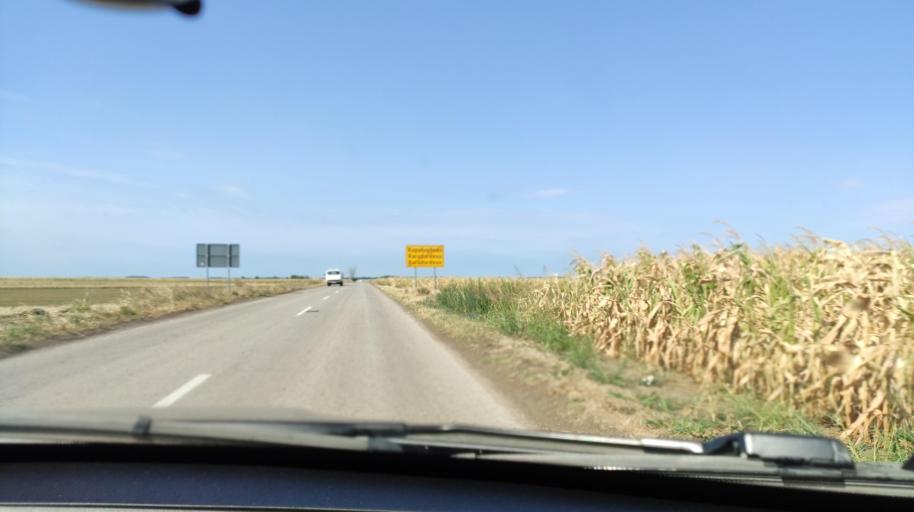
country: RS
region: Autonomna Pokrajina Vojvodina
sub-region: Severnobacki Okrug
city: Backa Topola
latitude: 45.8582
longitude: 19.5825
